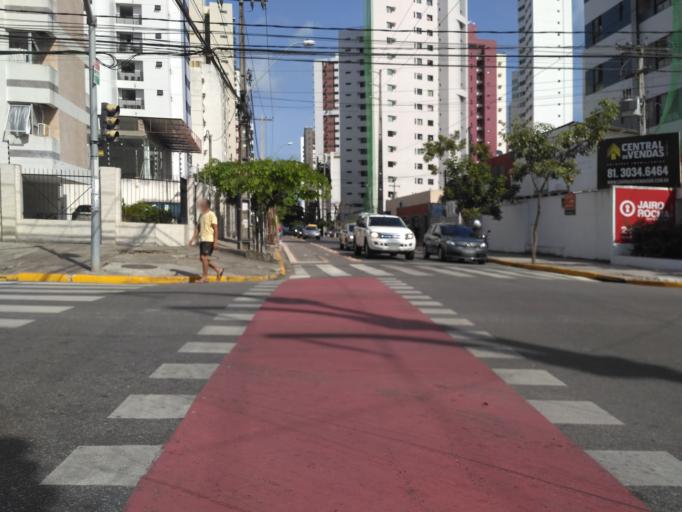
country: BR
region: Pernambuco
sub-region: Recife
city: Recife
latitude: -8.1422
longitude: -34.9087
